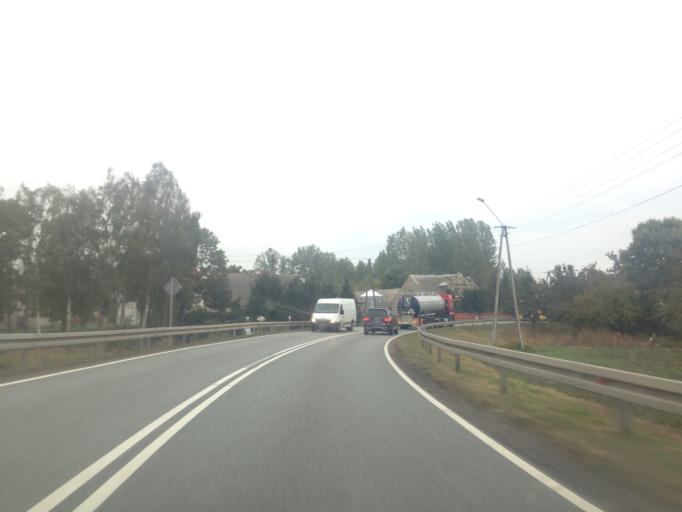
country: PL
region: Kujawsko-Pomorskie
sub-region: Powiat mogilenski
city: Mogilno
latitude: 52.6208
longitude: 18.0485
